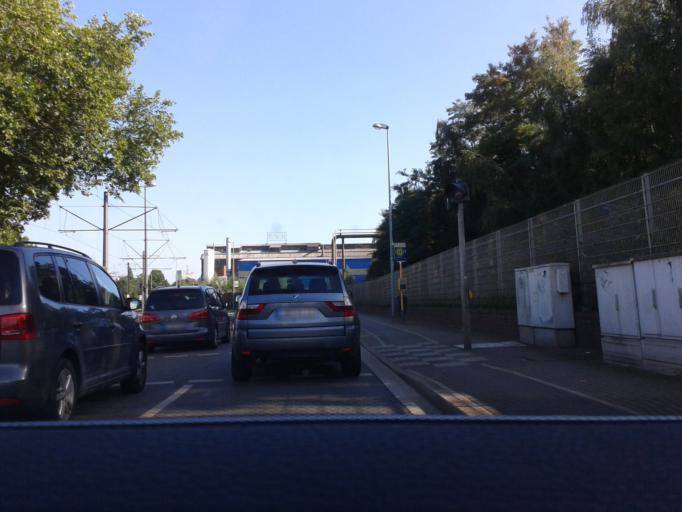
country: DE
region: North Rhine-Westphalia
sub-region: Regierungsbezirk Dusseldorf
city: Muelheim (Ruhr)
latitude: 51.4394
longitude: 6.8702
